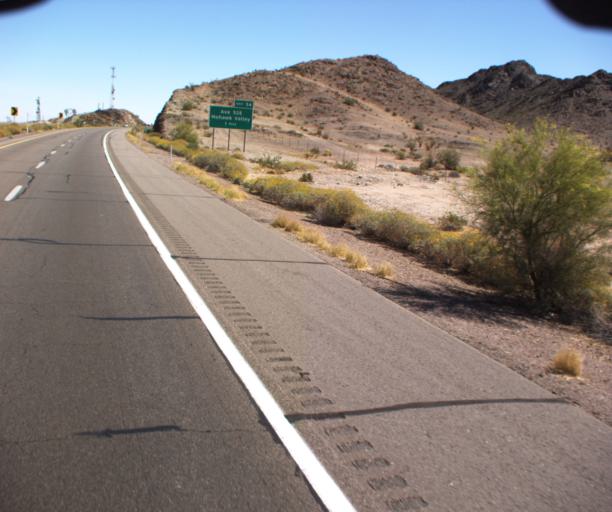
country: US
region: Arizona
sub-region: Yuma County
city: Wellton
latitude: 32.7251
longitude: -113.7533
